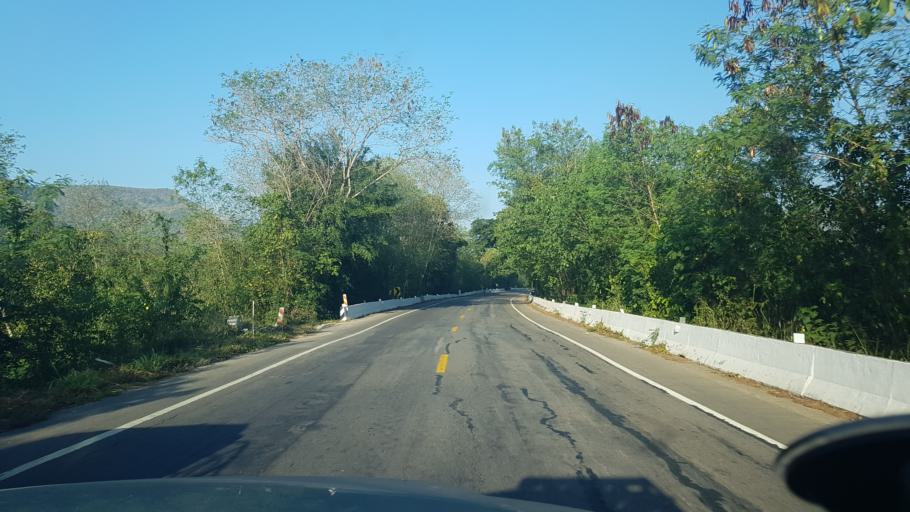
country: TH
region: Khon Kaen
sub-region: Amphoe Phu Pha Man
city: Phu Pha Man
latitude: 16.6474
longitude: 101.7804
